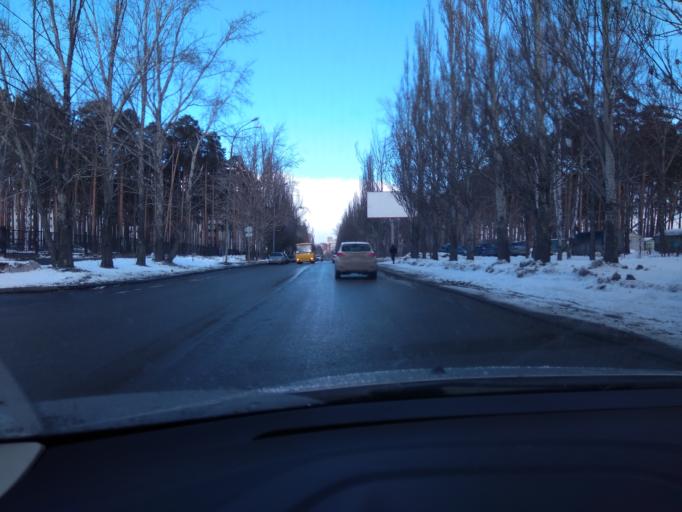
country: RU
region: Sverdlovsk
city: Sovkhoznyy
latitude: 56.8069
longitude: 60.5607
